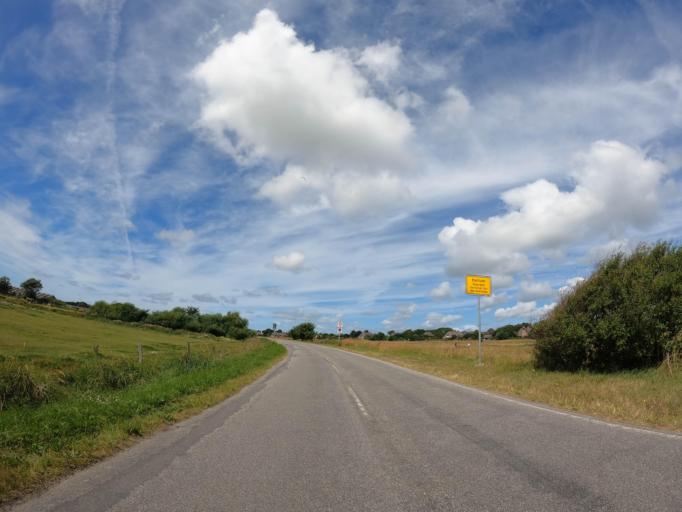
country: DE
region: Schleswig-Holstein
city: Keitum
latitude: 54.8868
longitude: 8.3790
